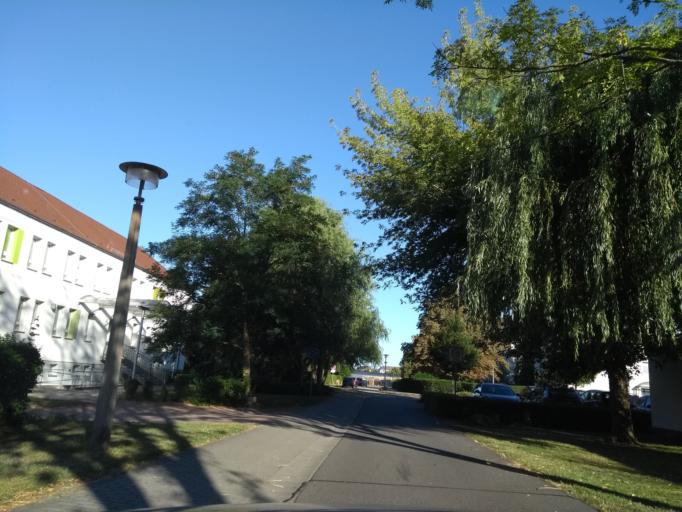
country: DE
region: Brandenburg
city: Lubbenau
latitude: 51.8565
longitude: 13.9603
